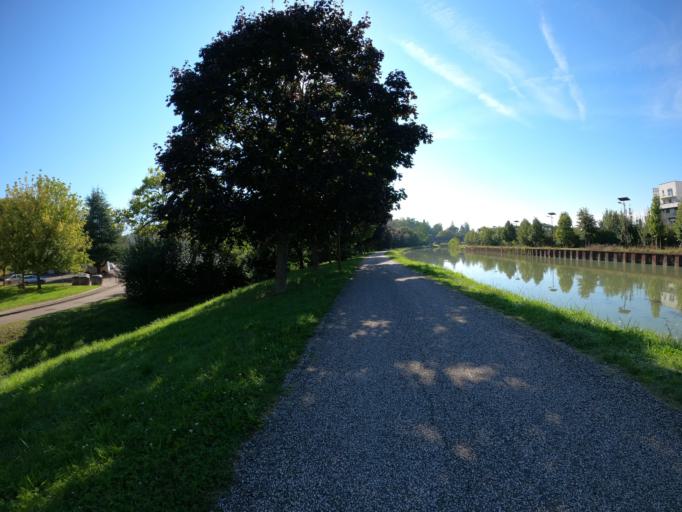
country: FR
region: Aquitaine
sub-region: Departement du Lot-et-Garonne
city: Agen
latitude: 44.2075
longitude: 0.6420
